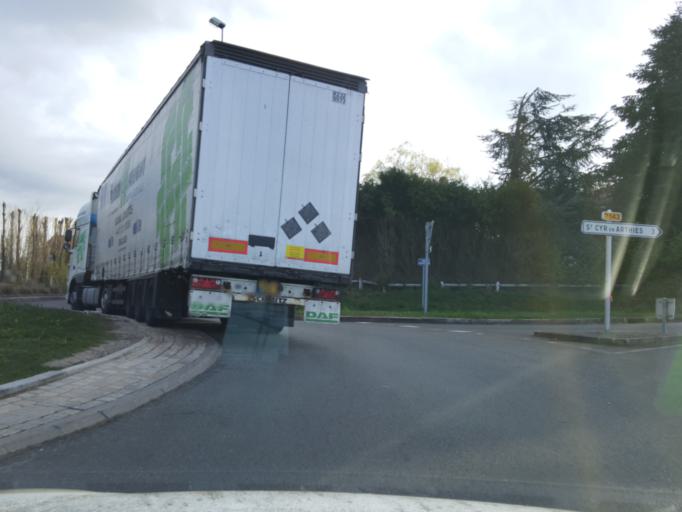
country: FR
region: Ile-de-France
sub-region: Departement des Yvelines
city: Follainville-Dennemont
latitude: 49.0575
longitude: 1.7716
